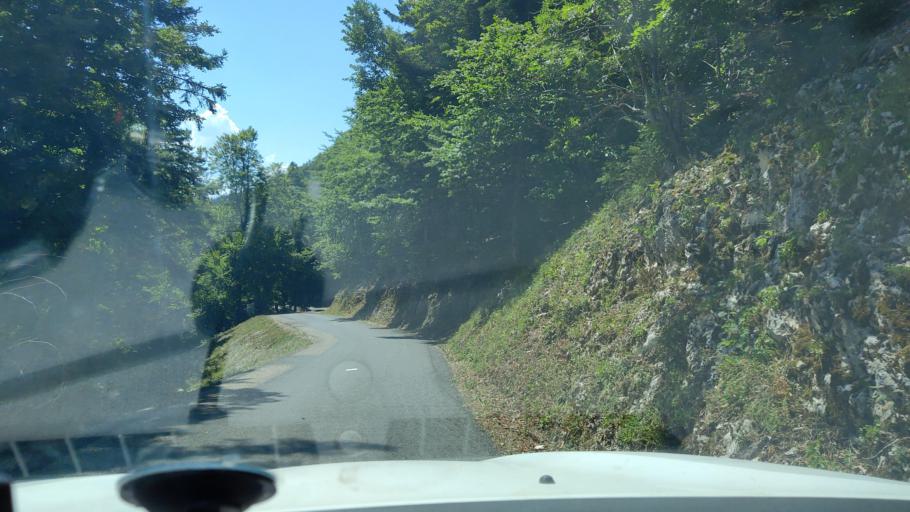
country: FR
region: Rhone-Alpes
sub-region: Departement de la Savoie
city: Le Bourget-du-Lac
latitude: 45.6498
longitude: 5.8242
